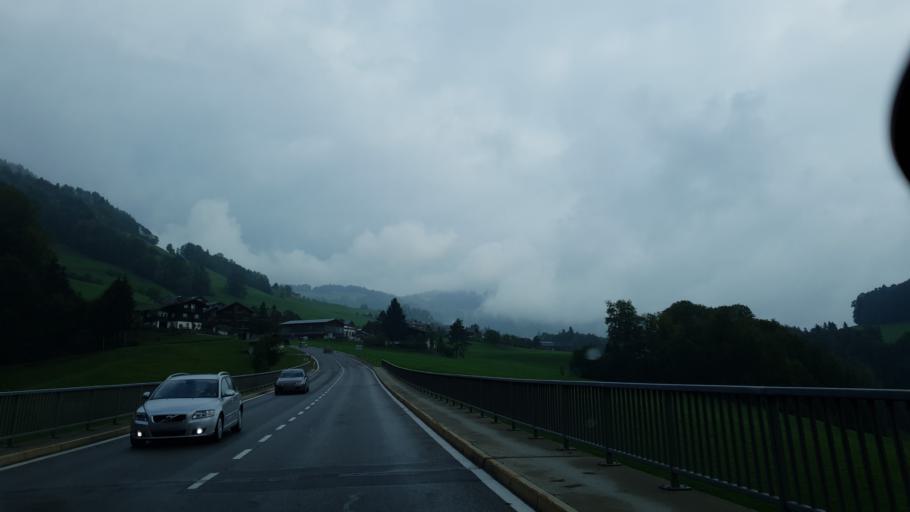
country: AT
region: Vorarlberg
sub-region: Politischer Bezirk Bregenz
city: Andelsbuch
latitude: 47.4010
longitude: 9.8515
